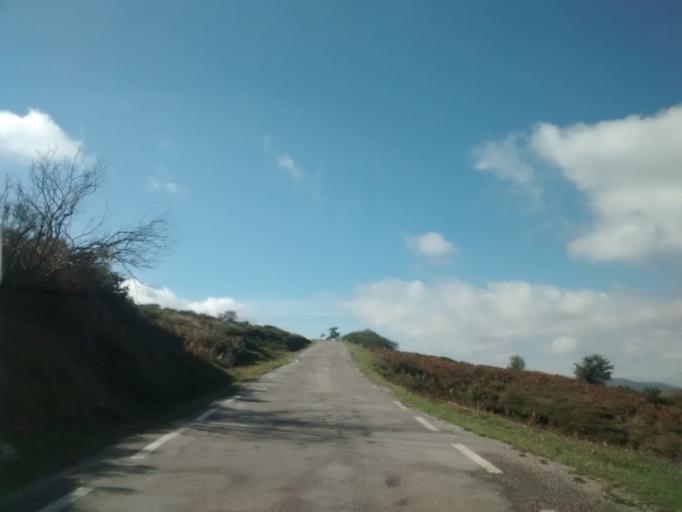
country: ES
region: Castille and Leon
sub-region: Provincia de Burgos
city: Arija
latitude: 42.9267
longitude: -3.9910
